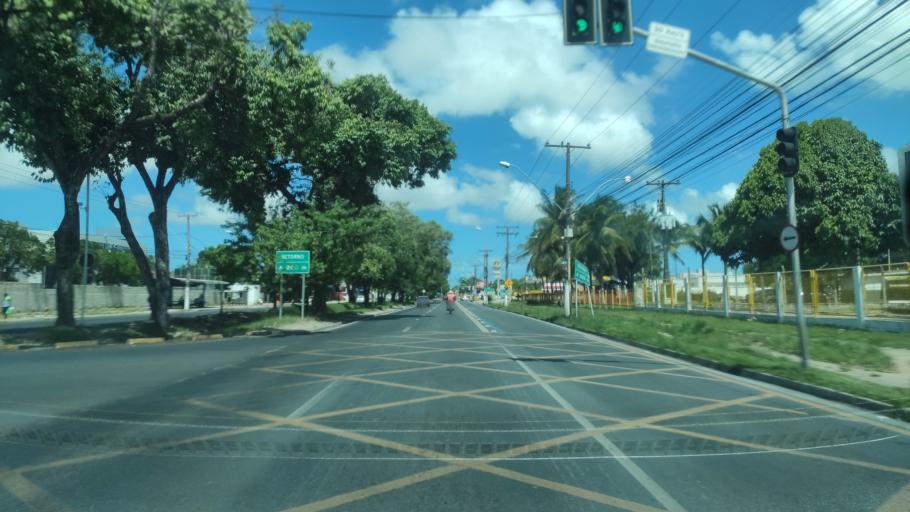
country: BR
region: Alagoas
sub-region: Satuba
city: Satuba
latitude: -9.5844
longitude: -35.7647
